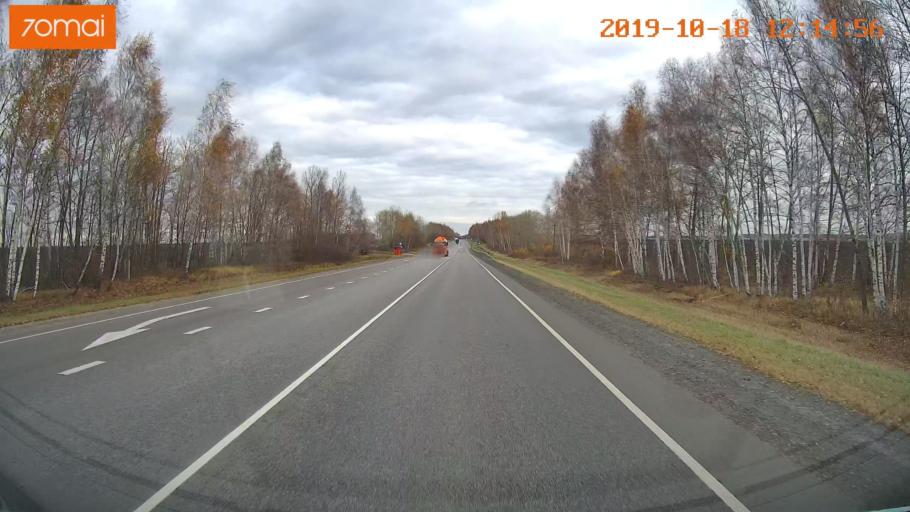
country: RU
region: Rjazan
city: Zakharovo
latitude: 54.4371
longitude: 39.3916
